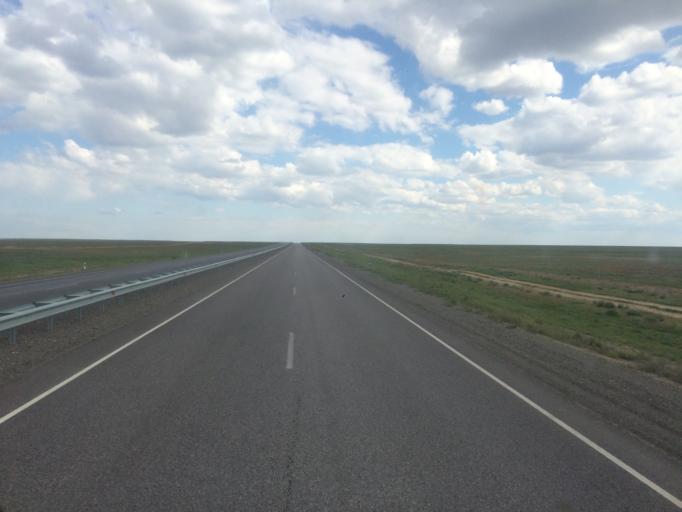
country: KZ
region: Qyzylorda
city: Shalqiya
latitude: 43.7383
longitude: 67.5254
